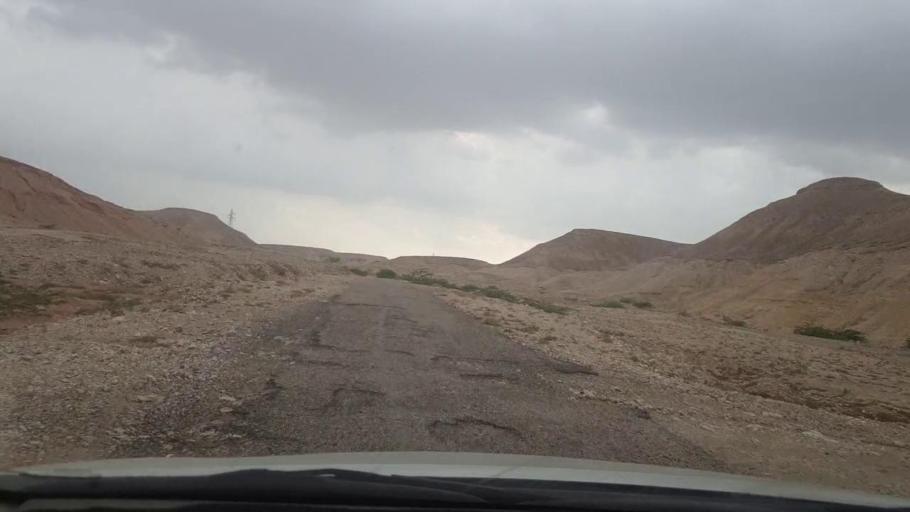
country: PK
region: Sindh
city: Khairpur
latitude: 27.4708
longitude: 68.9122
